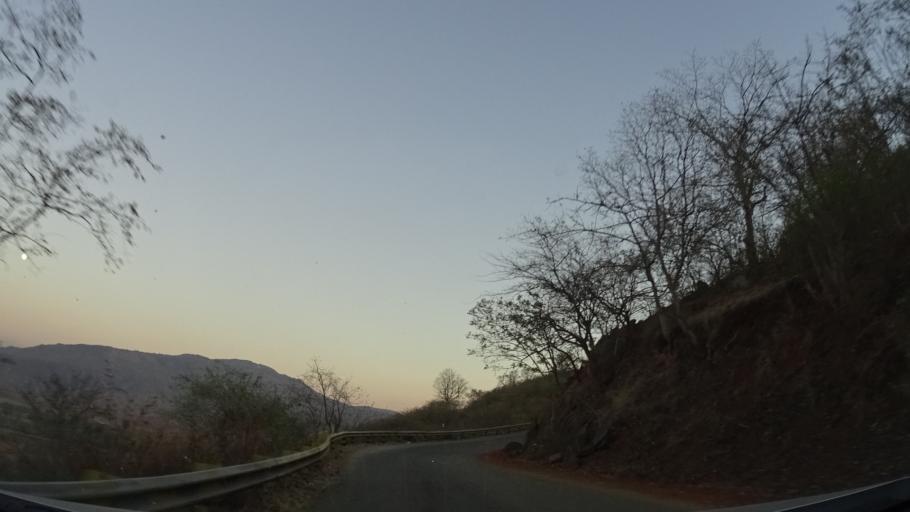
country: IN
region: Karnataka
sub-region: Chikmagalur
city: Birur
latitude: 13.5503
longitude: 75.8219
